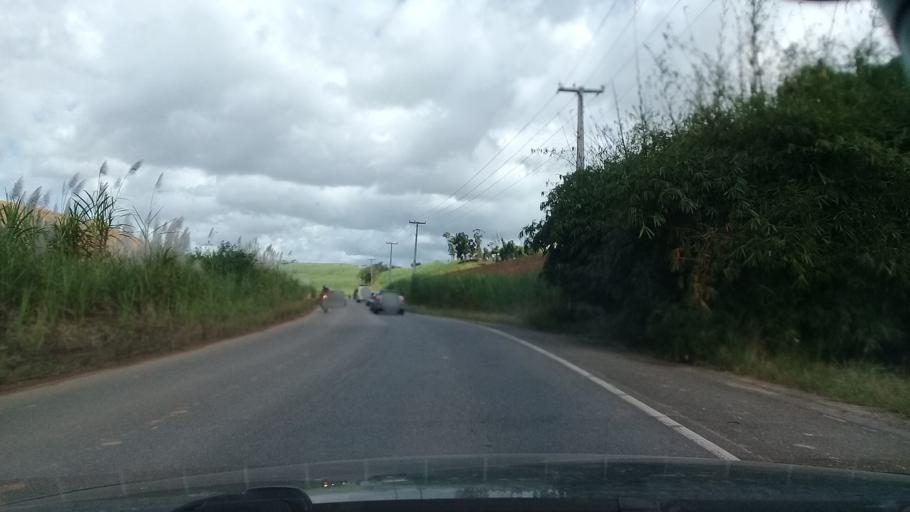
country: BR
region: Pernambuco
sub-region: Ipojuca
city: Ipojuca
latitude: -8.4438
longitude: -35.0906
